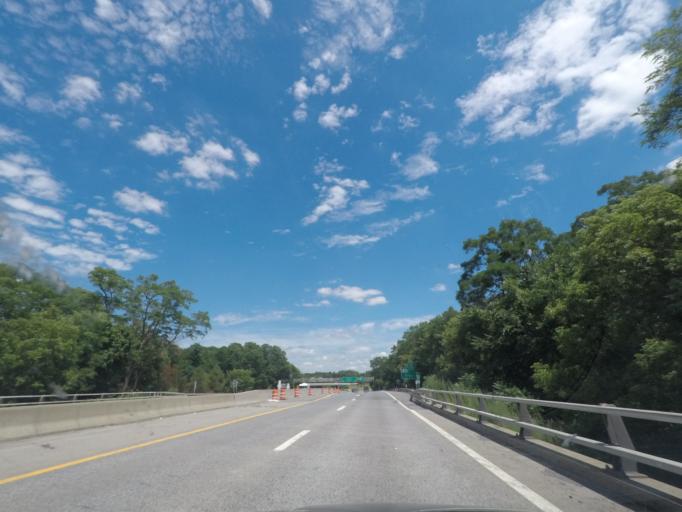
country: US
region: New York
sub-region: Schenectady County
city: Schenectady
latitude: 42.7788
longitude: -73.9242
